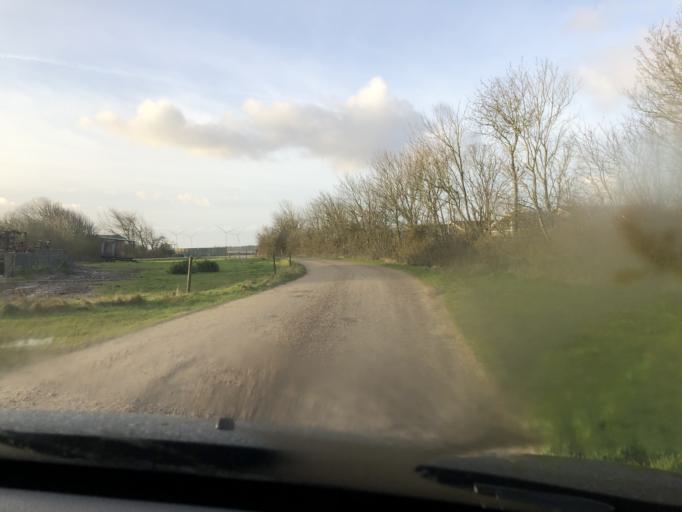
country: DK
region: Central Jutland
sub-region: Ringkobing-Skjern Kommune
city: Skjern
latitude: 55.8749
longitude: 8.3465
